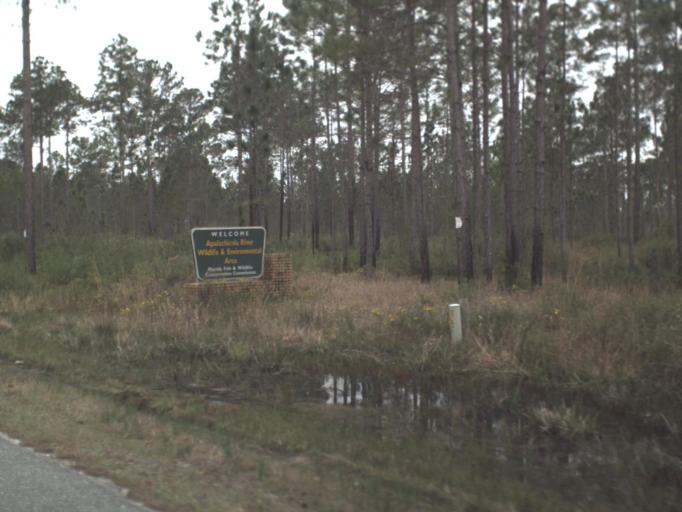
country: US
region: Florida
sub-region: Franklin County
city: Apalachicola
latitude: 29.9031
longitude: -84.9778
